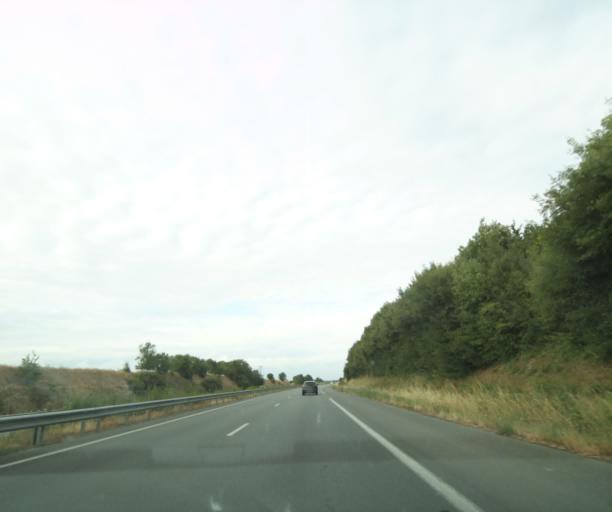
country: FR
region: Poitou-Charentes
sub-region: Departement de la Charente-Maritime
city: Dompierre-sur-Mer
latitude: 46.1909
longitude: -1.0698
